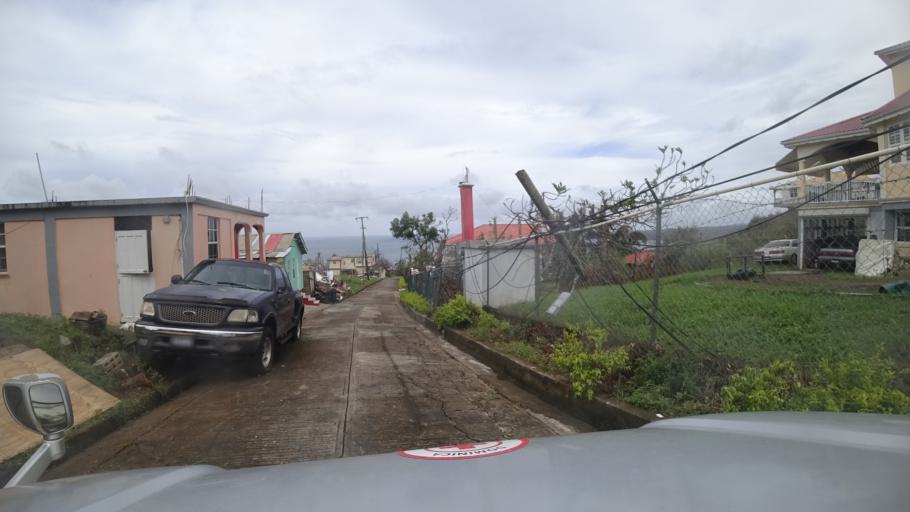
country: DM
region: Saint John
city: Portsmouth
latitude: 15.6142
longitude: -61.4100
